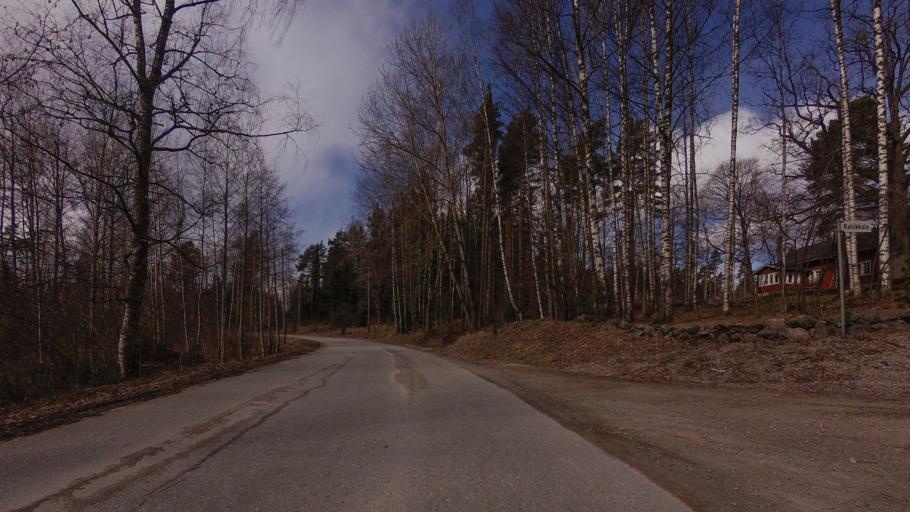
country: FI
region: Uusimaa
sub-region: Helsinki
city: Karjalohja
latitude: 60.2624
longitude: 23.7100
